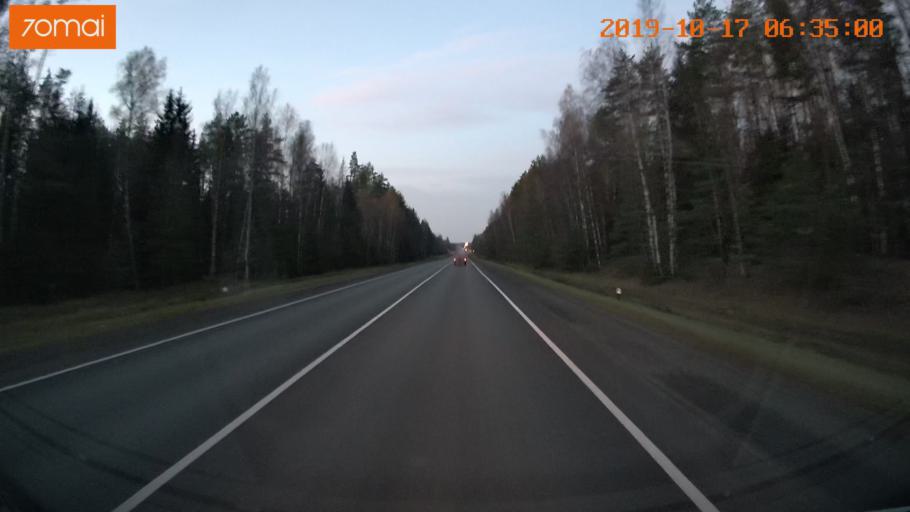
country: RU
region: Ivanovo
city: Novoye Leushino
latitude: 56.6969
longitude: 40.6287
